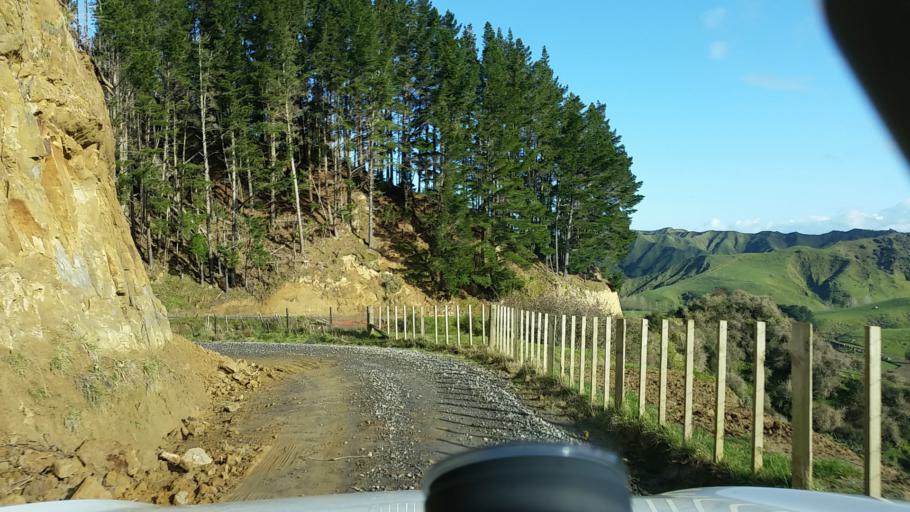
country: NZ
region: Taranaki
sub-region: South Taranaki District
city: Eltham
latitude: -39.4087
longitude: 174.5369
